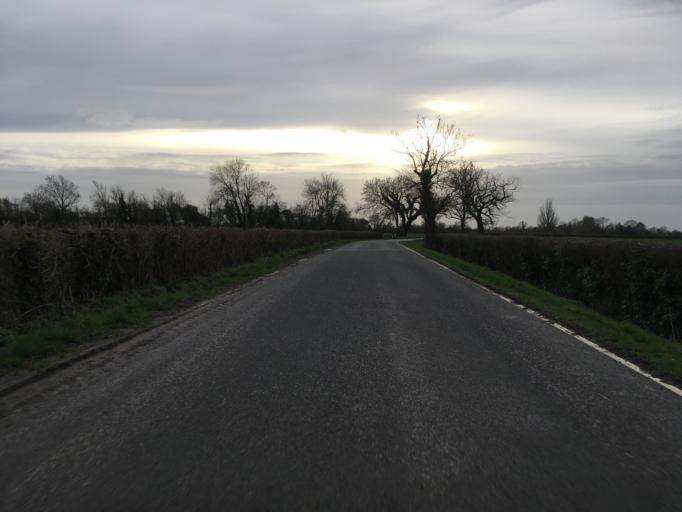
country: GB
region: Wales
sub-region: Newport
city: Redwick
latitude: 51.5595
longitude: -2.8330
